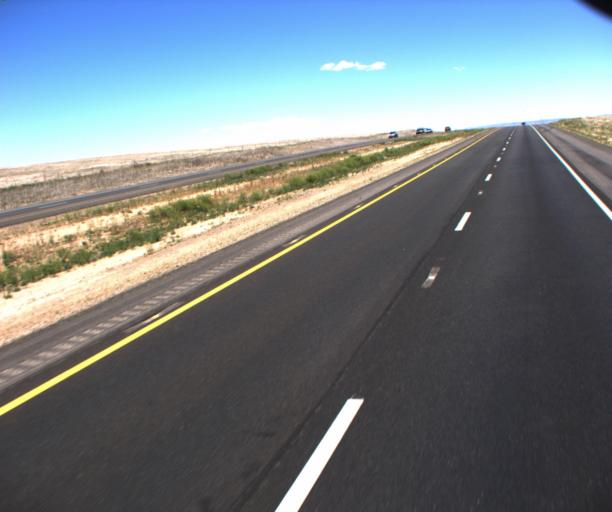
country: US
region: Arizona
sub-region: Yavapai County
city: Chino Valley
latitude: 34.6926
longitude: -112.4467
